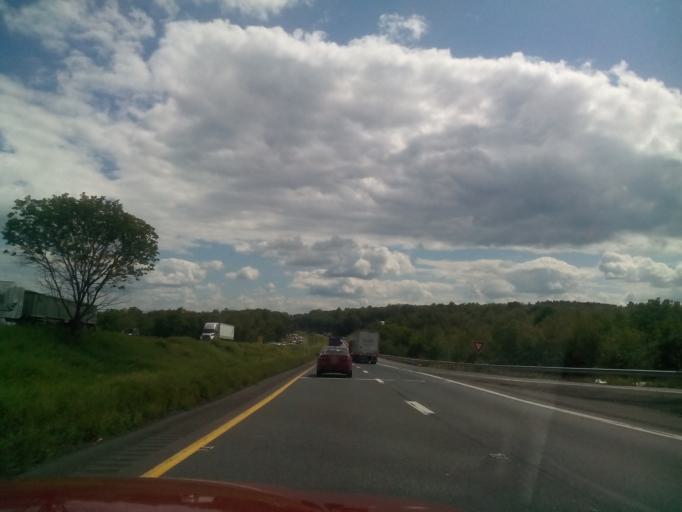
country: US
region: Pennsylvania
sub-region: Monroe County
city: Tannersville
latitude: 41.0366
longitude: -75.3118
